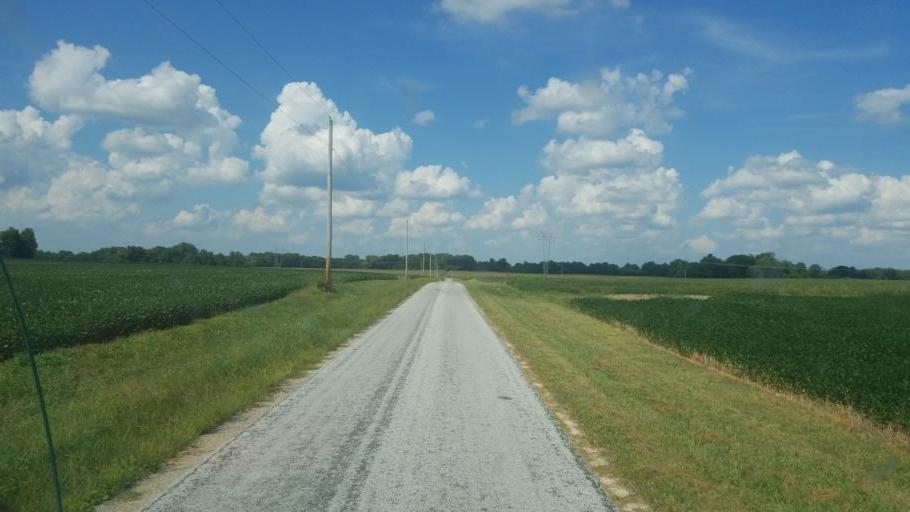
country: US
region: Ohio
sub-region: Wyandot County
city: Carey
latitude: 40.9670
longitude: -83.2471
